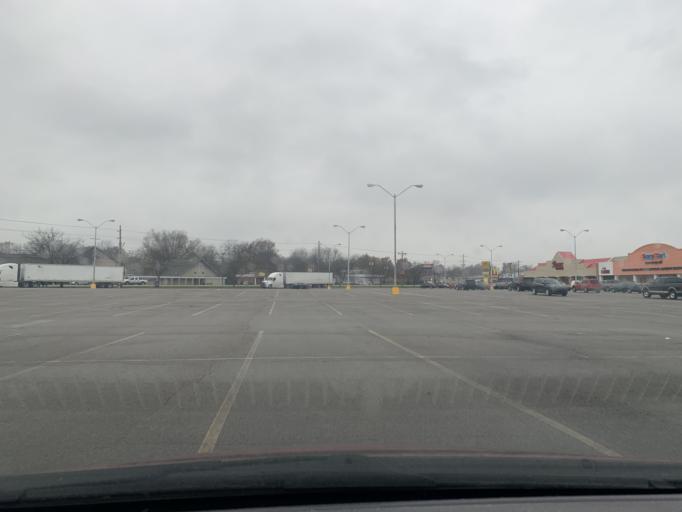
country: US
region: Kentucky
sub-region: Jefferson County
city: Okolona
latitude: 38.1672
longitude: -85.7032
